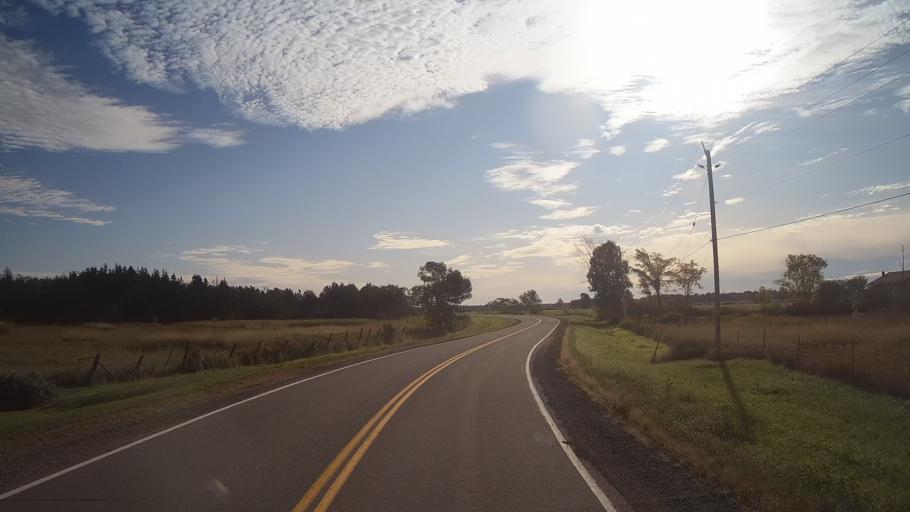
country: CA
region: Ontario
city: Gananoque
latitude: 44.3878
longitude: -76.1302
